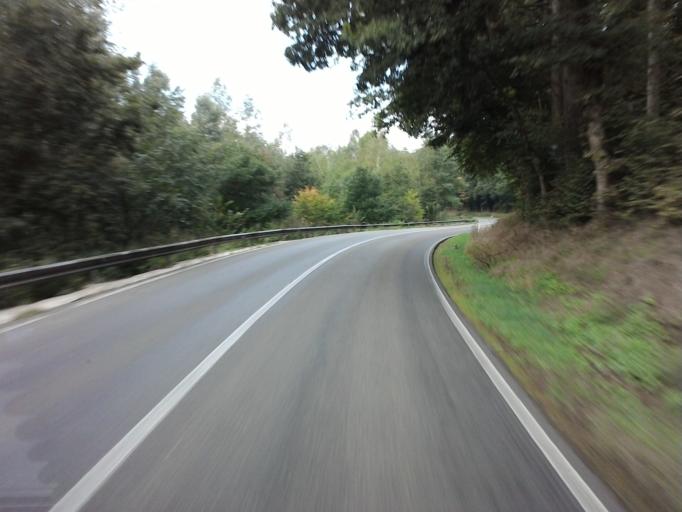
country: BE
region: Wallonia
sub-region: Province du Luxembourg
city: Saint-Leger
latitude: 49.5904
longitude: 5.6312
